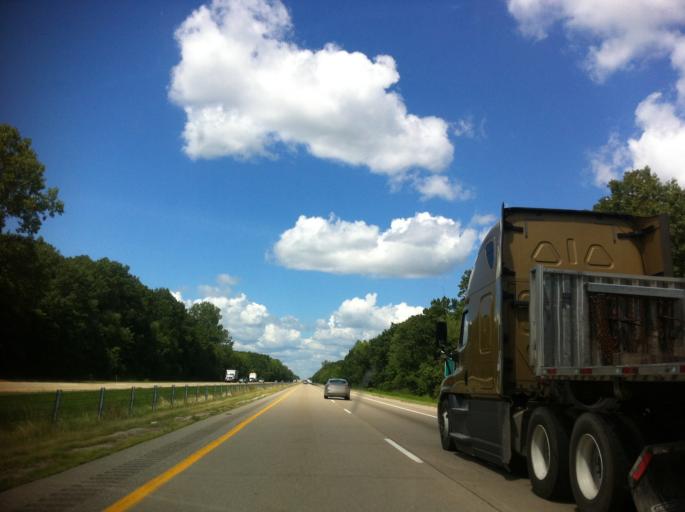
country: US
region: Michigan
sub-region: Monroe County
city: Petersburg
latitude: 41.8904
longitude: -83.6613
